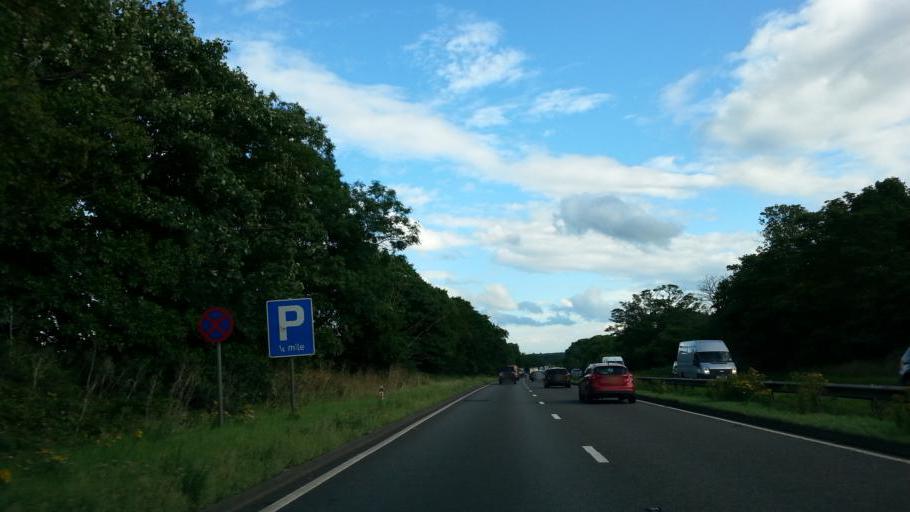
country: GB
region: England
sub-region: Nottinghamshire
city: Bircotes
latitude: 53.3544
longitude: -1.0389
